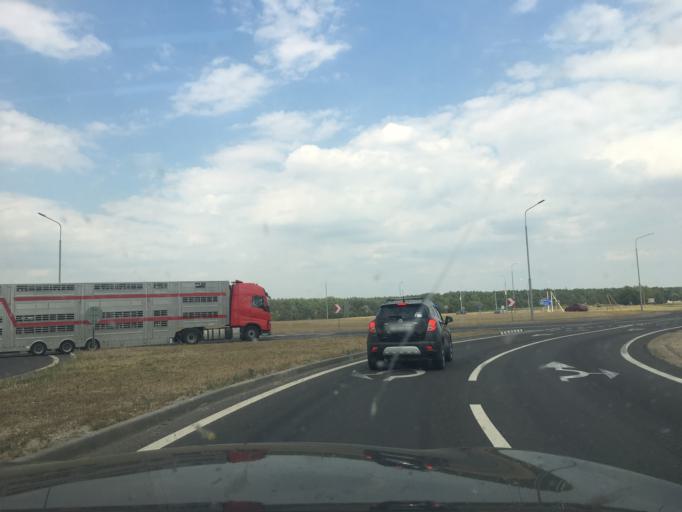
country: BY
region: Brest
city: Brest
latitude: 52.1512
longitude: 23.6902
